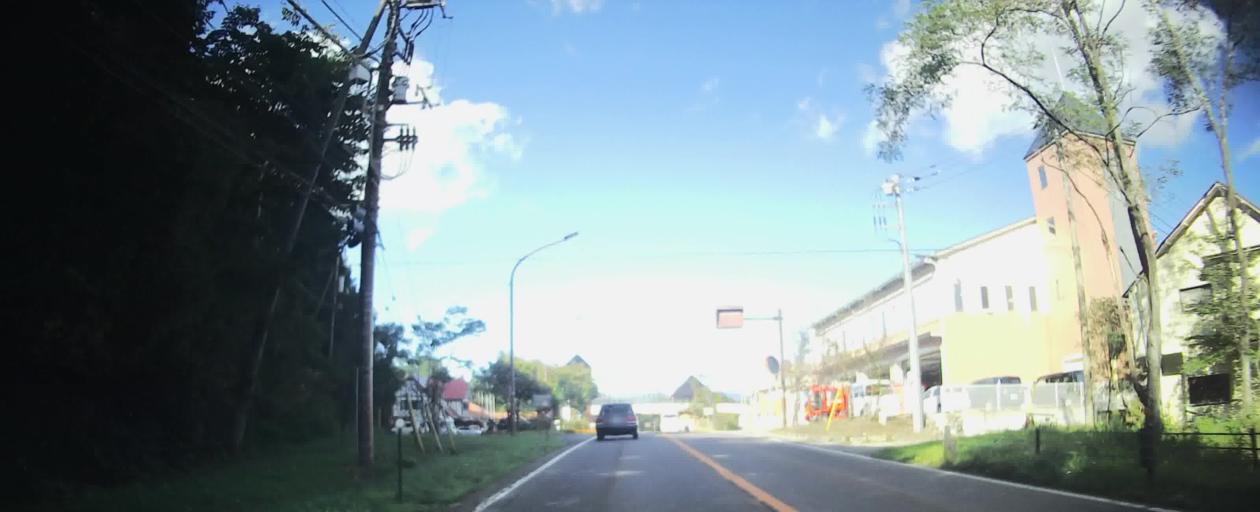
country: JP
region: Gunma
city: Nakanojomachi
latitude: 36.6137
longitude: 138.5897
